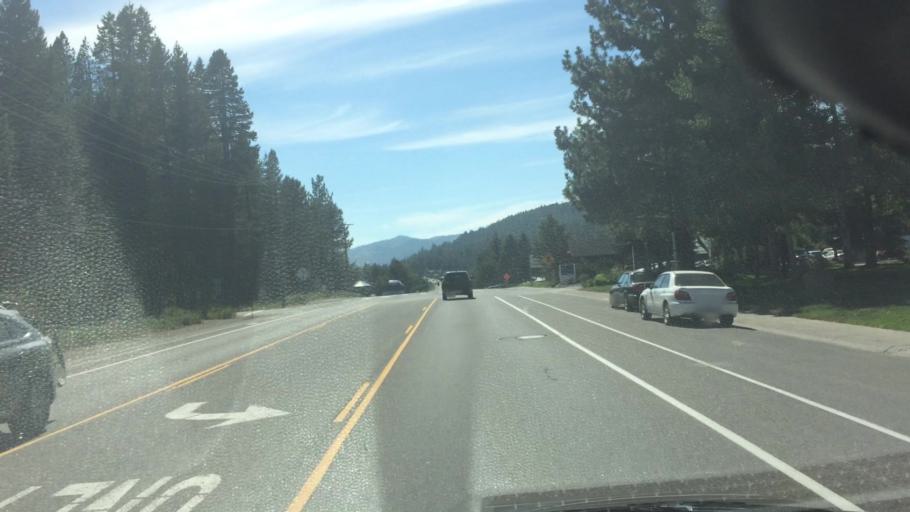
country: US
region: California
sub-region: Nevada County
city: Truckee
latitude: 39.3261
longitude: -120.2040
